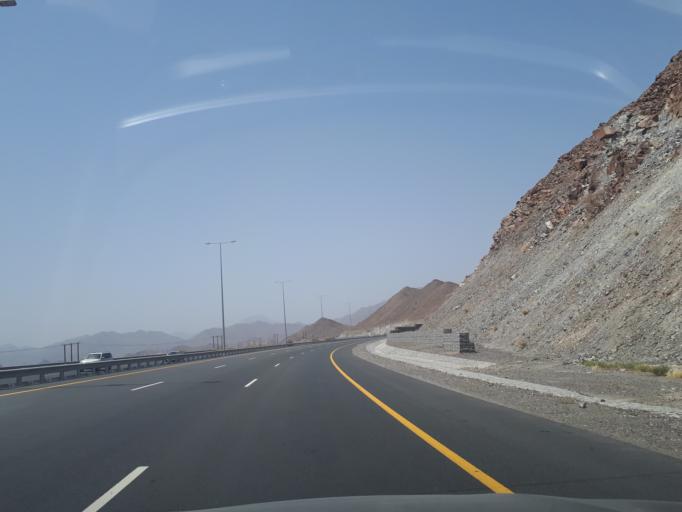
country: OM
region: Muhafazat ad Dakhiliyah
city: Bidbid
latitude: 23.3166
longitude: 58.1141
